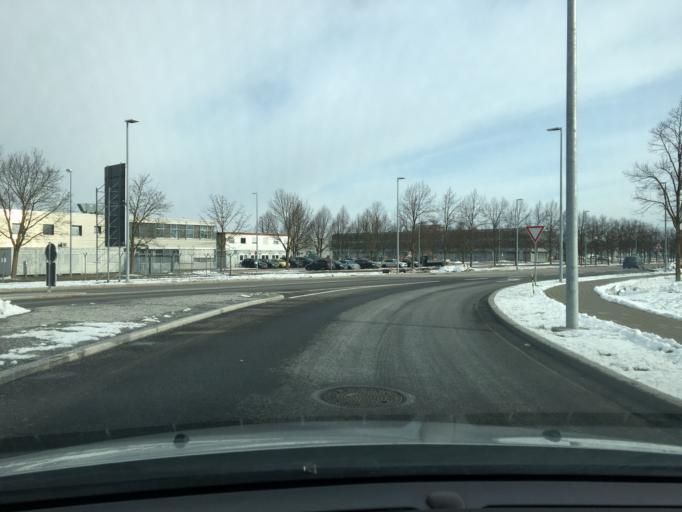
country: DE
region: Bavaria
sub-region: Upper Bavaria
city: Hallbergmoos
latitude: 48.3551
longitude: 11.7601
